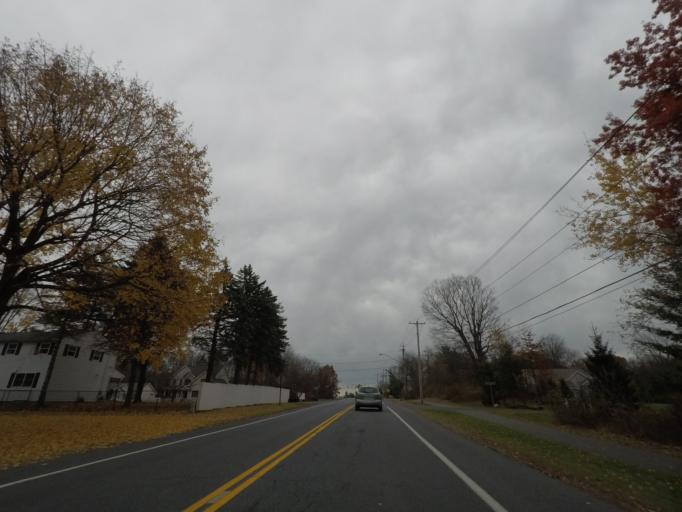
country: US
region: New York
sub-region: Schenectady County
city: Niskayuna
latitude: 42.8188
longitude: -73.7779
